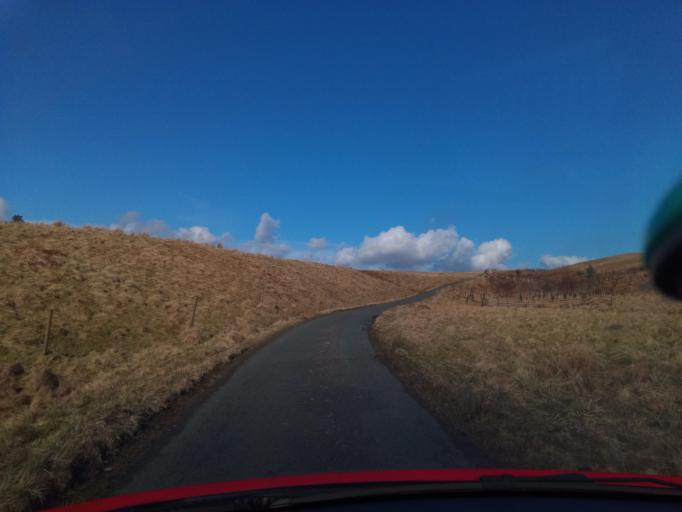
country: GB
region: Scotland
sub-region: The Scottish Borders
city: Hawick
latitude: 55.4310
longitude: -2.8768
